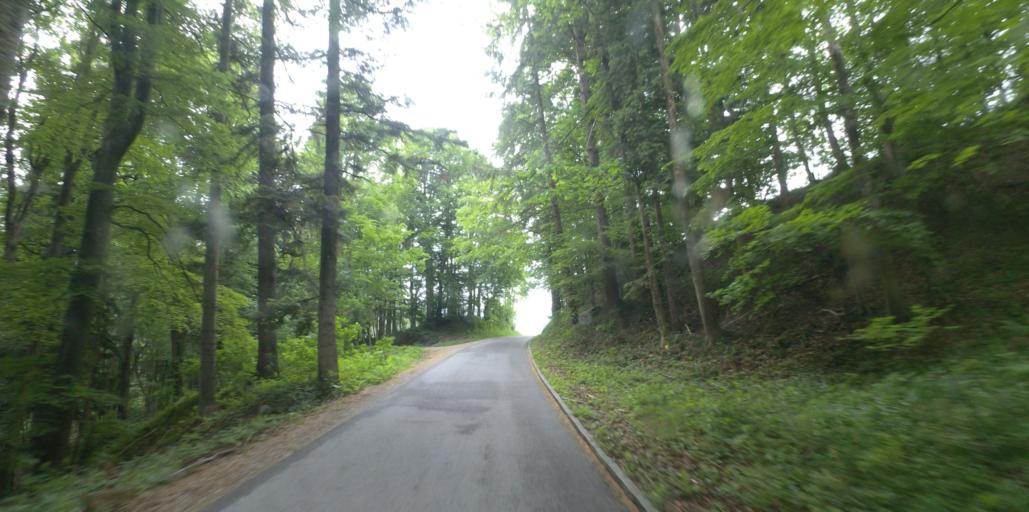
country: DE
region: Bavaria
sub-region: Upper Bavaria
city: Bernau am Chiemsee
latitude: 47.7892
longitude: 12.3643
